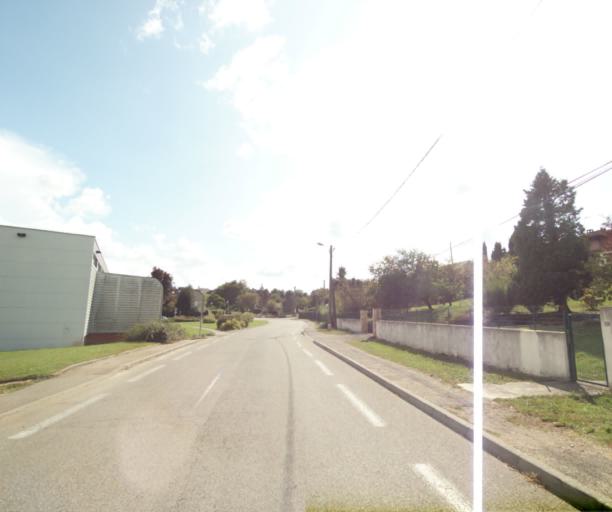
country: FR
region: Bourgogne
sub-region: Departement de Saone-et-Loire
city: Tournus
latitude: 46.5727
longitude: 4.9087
